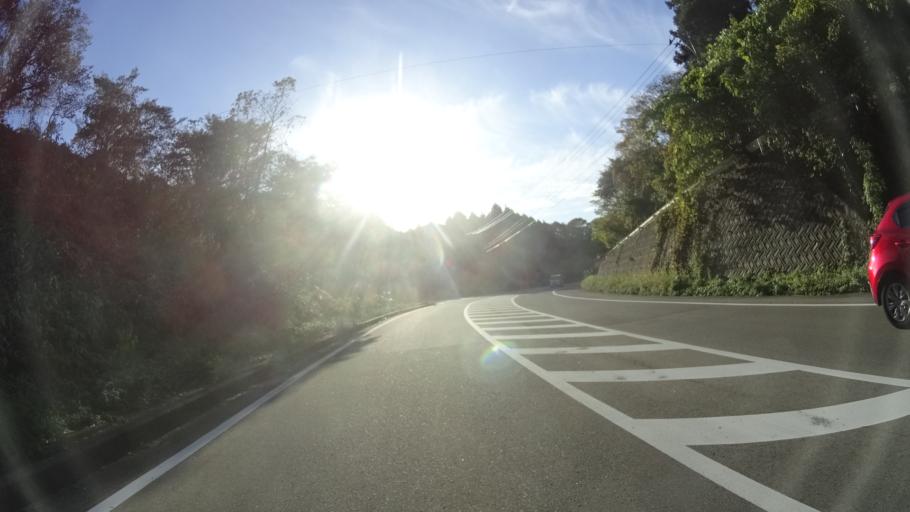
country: JP
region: Ishikawa
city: Hakui
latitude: 37.0049
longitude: 136.8084
